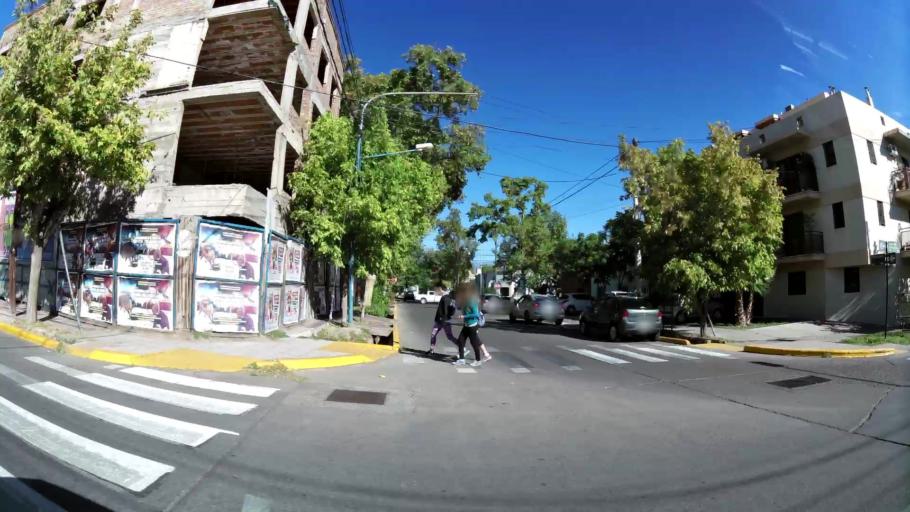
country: AR
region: Mendoza
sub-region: Departamento de Godoy Cruz
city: Godoy Cruz
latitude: -32.9238
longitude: -68.8426
